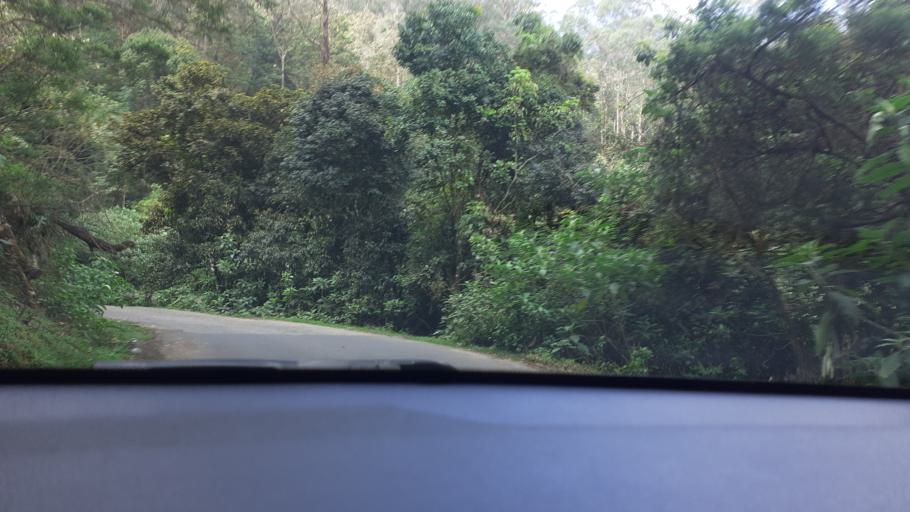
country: IN
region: Tamil Nadu
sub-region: Dindigul
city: Kodaikanal
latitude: 10.2369
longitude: 77.4233
